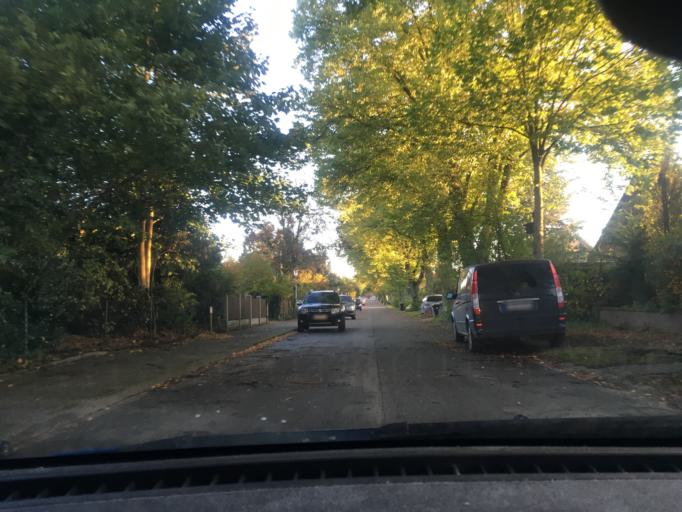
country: DE
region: Lower Saxony
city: Deutsch Evern
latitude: 53.2057
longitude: 10.4384
